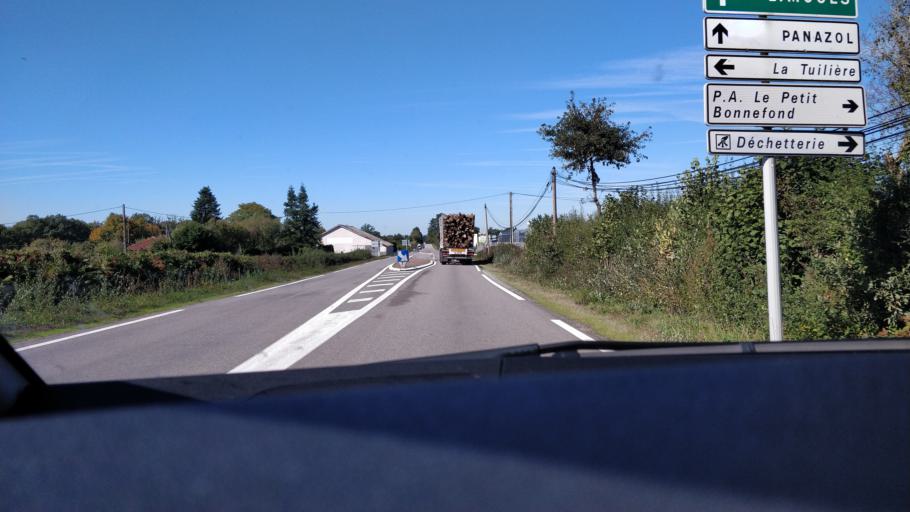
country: FR
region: Limousin
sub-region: Departement de la Haute-Vienne
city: Saint-Just-le-Martel
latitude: 45.8463
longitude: 1.3714
